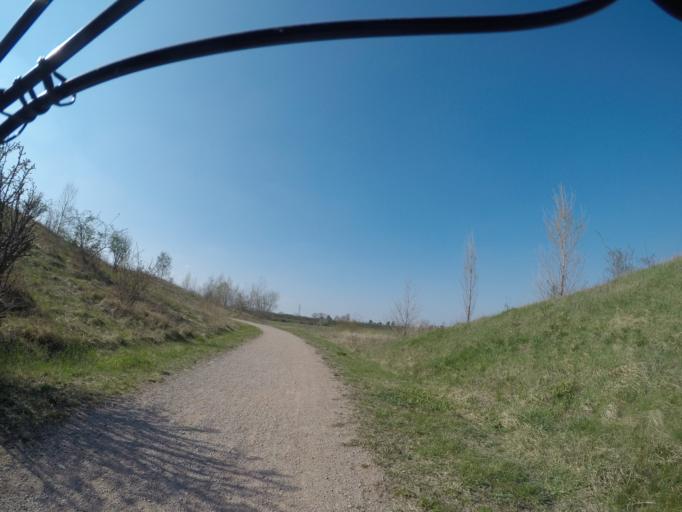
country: AT
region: Lower Austria
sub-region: Politischer Bezirk Modling
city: Laxenburg
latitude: 48.0621
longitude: 16.3452
